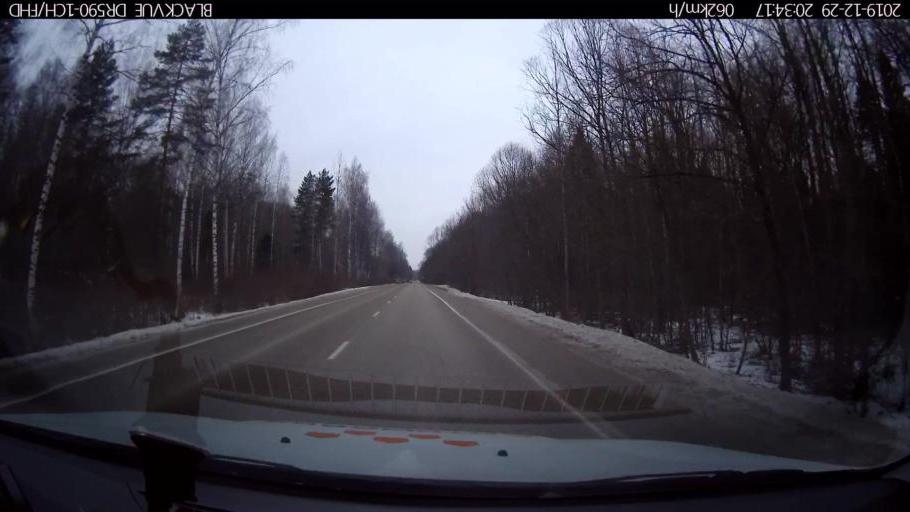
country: RU
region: Nizjnij Novgorod
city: Afonino
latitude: 56.1852
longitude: 44.0415
